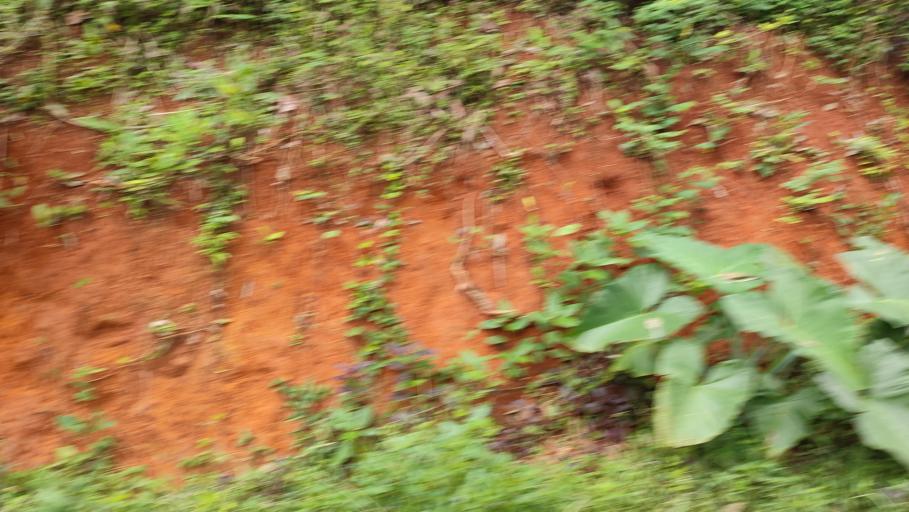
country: IN
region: Kerala
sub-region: Kasaragod District
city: Nileshwar
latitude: 12.2974
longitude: 75.2930
